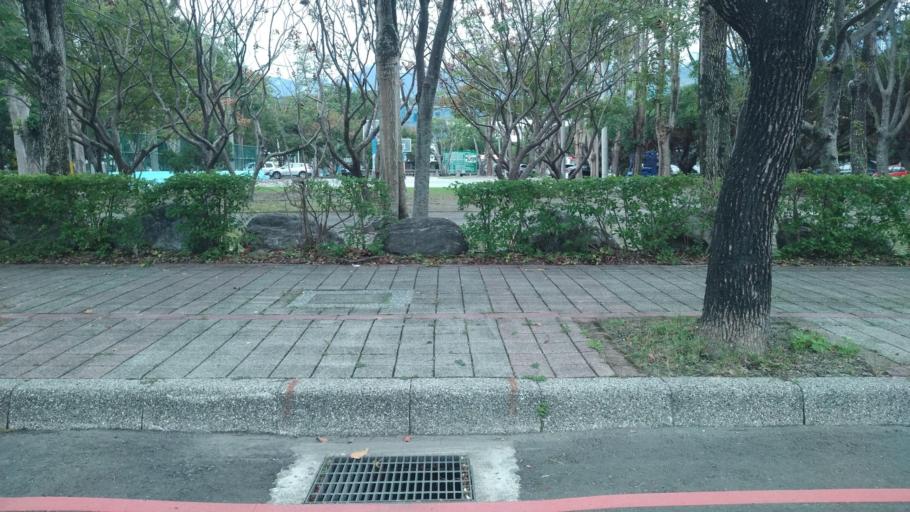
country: TW
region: Taiwan
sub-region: Hualien
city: Hualian
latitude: 23.9928
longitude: 121.6219
